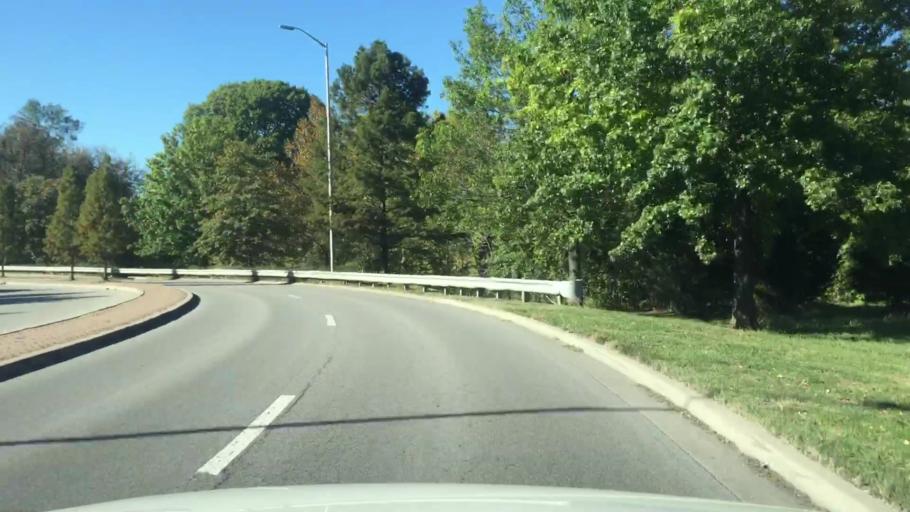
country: US
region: Kansas
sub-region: Johnson County
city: Leawood
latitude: 38.9281
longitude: -94.6252
